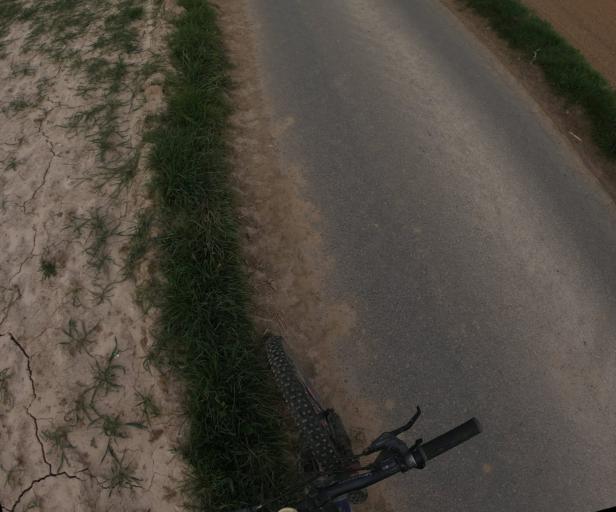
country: BE
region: Flanders
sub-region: Provincie Vlaams-Brabant
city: Lennik
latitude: 50.7903
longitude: 4.1669
